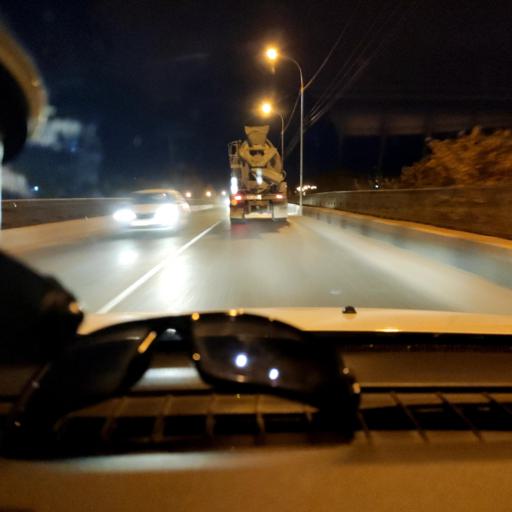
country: RU
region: Samara
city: Novokuybyshevsk
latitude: 53.1154
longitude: 50.0624
